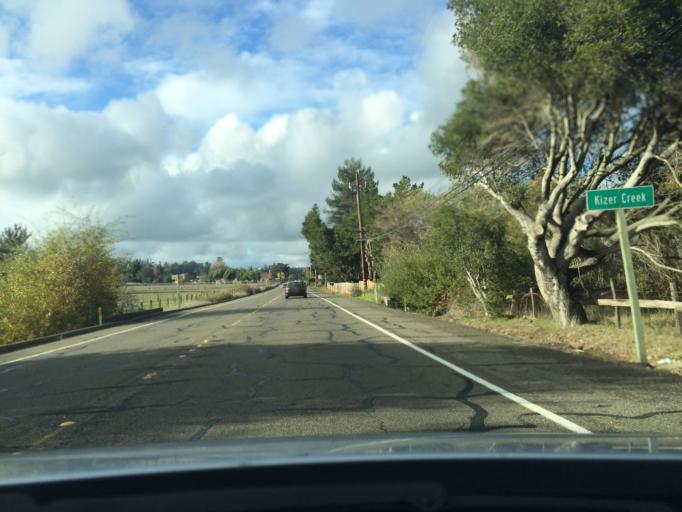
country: US
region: California
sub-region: Sonoma County
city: Penngrove
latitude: 38.2513
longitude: -122.6978
